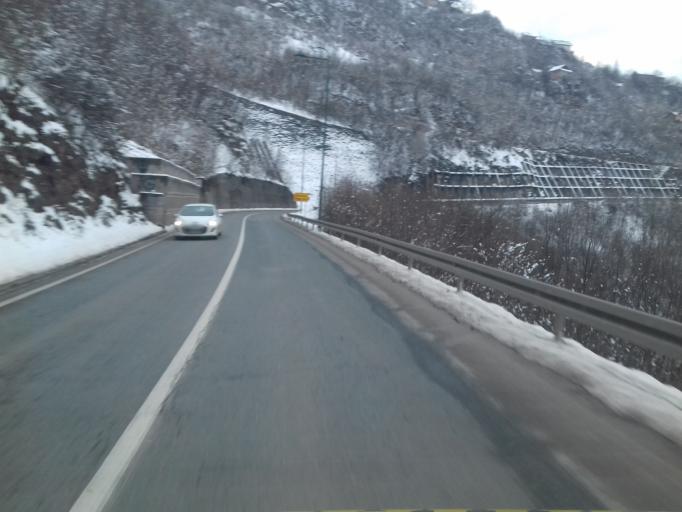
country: BA
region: Federation of Bosnia and Herzegovina
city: Kobilja Glava
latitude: 43.8565
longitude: 18.4488
